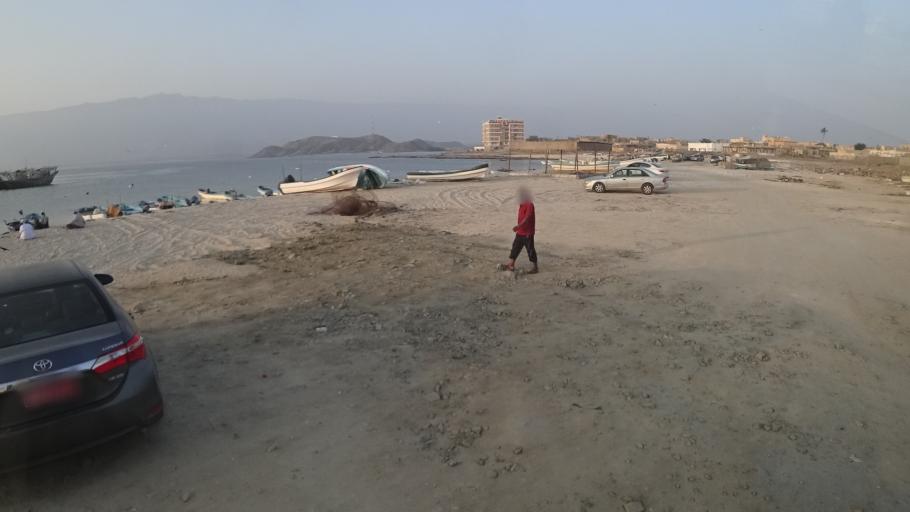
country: OM
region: Zufar
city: Salalah
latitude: 16.9858
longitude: 54.6875
